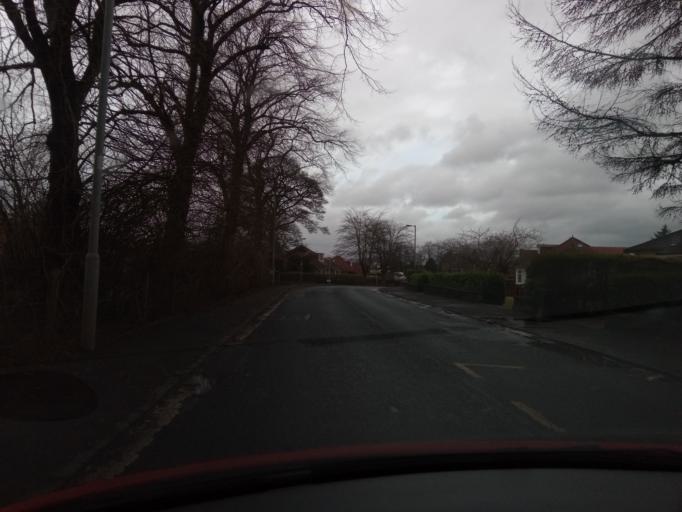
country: GB
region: Scotland
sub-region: East Dunbartonshire
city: Kirkintilloch
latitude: 55.9263
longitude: -4.1560
